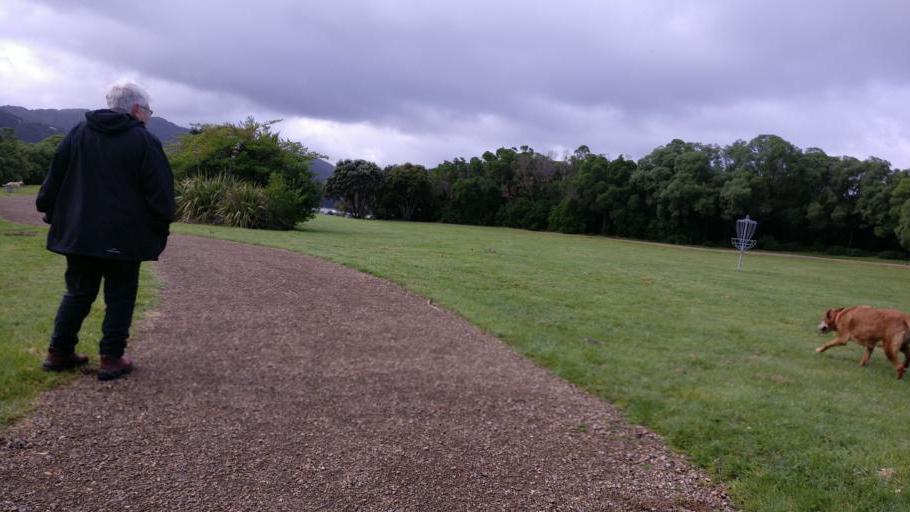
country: NZ
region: Wellington
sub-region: Lower Hutt City
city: Lower Hutt
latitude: -41.2365
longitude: 174.8987
